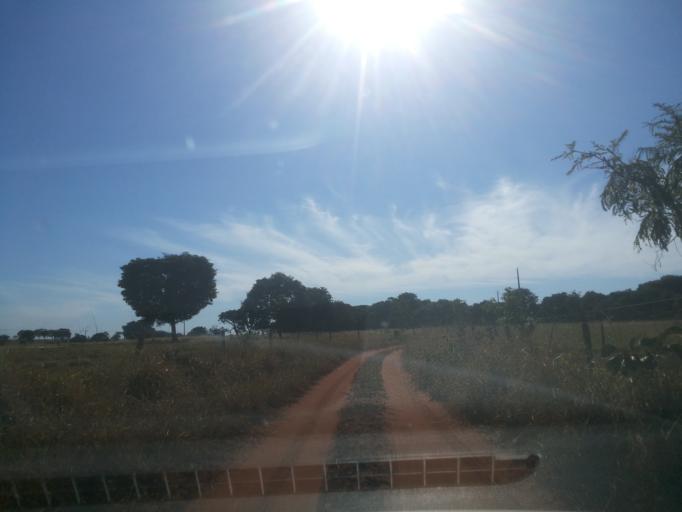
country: BR
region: Minas Gerais
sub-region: Ituiutaba
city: Ituiutaba
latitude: -19.1207
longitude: -49.3848
